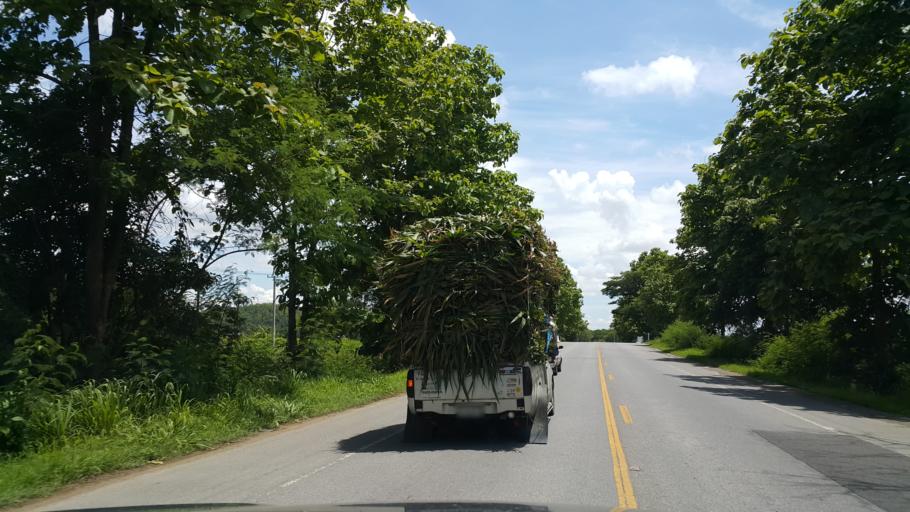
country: TH
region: Chiang Mai
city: San Kamphaeng
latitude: 18.7314
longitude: 99.1912
